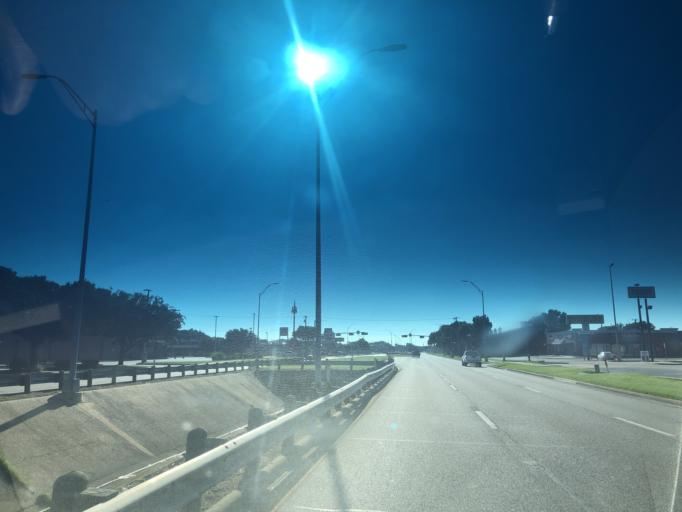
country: US
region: Texas
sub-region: Dallas County
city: Grand Prairie
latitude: 32.7093
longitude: -97.0005
